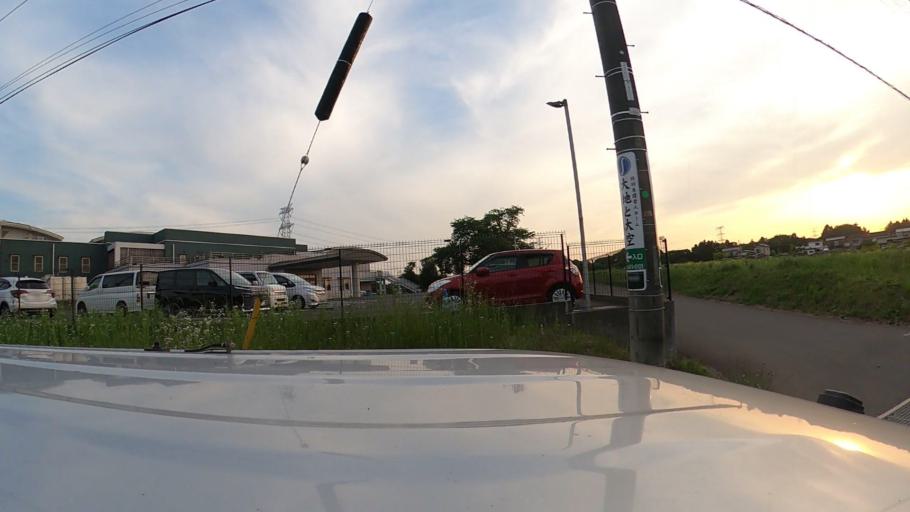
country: JP
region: Ibaraki
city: Ushiku
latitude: 36.0074
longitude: 140.1145
